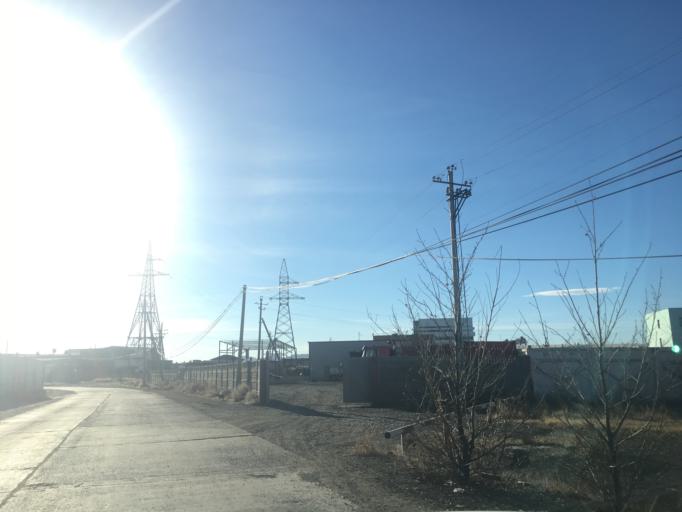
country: MN
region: Ulaanbaatar
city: Ulaanbaatar
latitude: 47.9021
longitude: 106.7981
